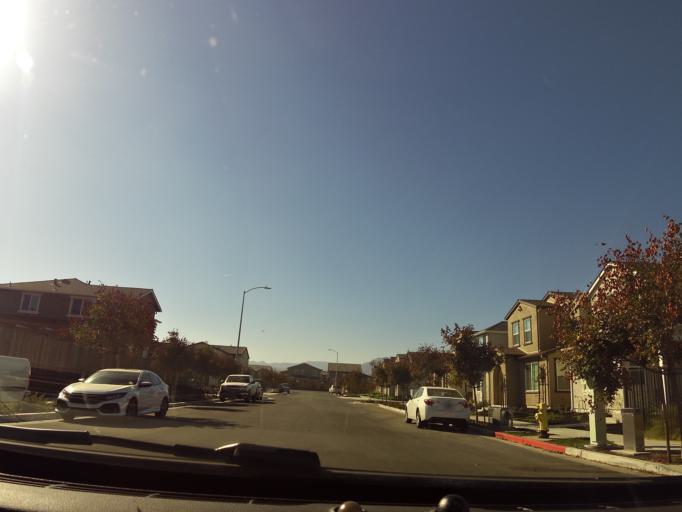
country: US
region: California
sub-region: San Benito County
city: Hollister
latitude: 36.8317
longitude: -121.3991
